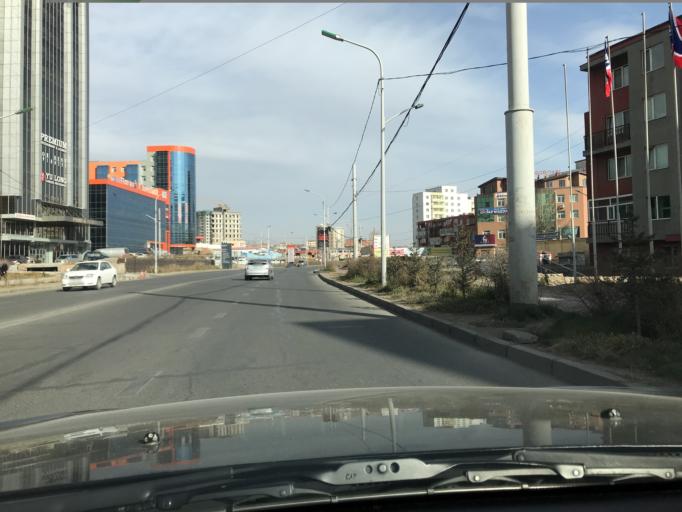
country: MN
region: Ulaanbaatar
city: Ulaanbaatar
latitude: 47.9238
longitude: 106.9014
